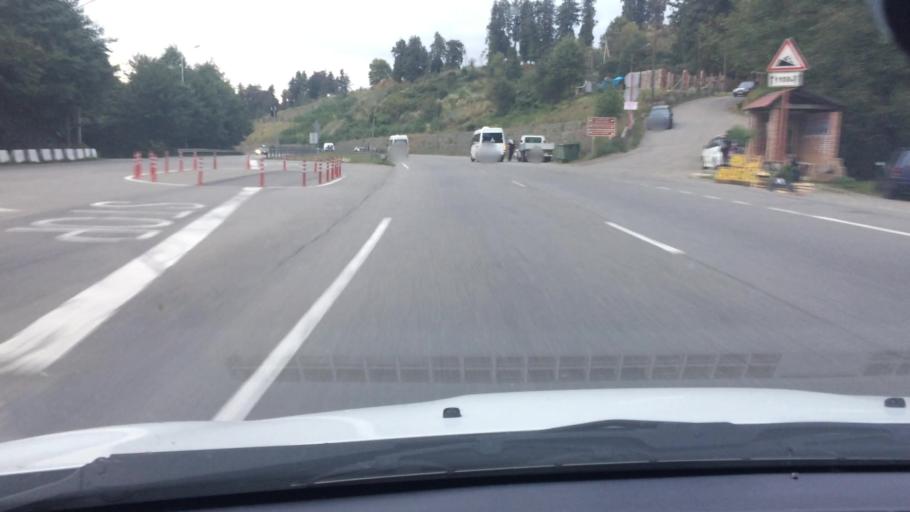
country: GE
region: Ajaria
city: Makhinjauri
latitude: 41.6939
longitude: 41.7250
